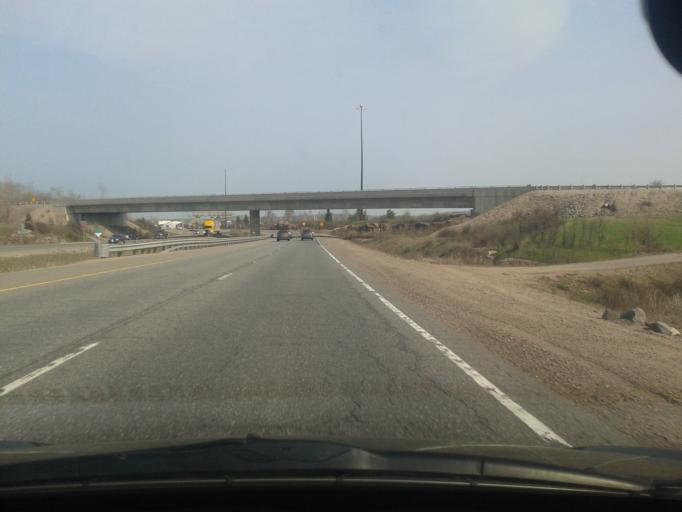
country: CA
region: Ontario
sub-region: Nipissing District
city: North Bay
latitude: 46.3043
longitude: -79.4313
